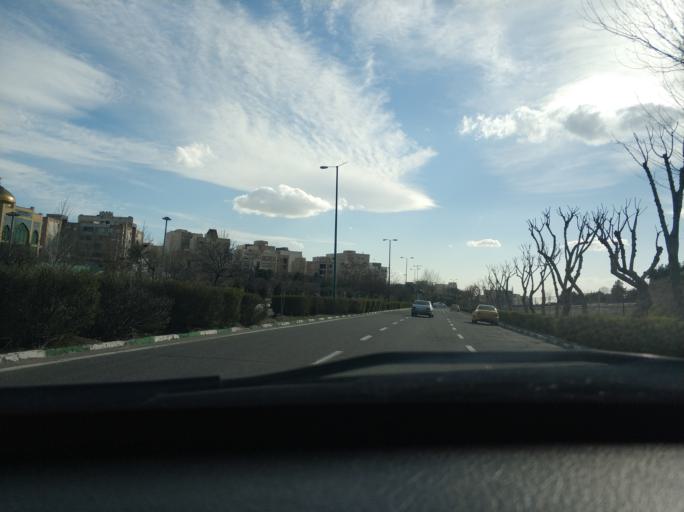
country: IR
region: Tehran
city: Tajrish
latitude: 35.7451
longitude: 51.5993
